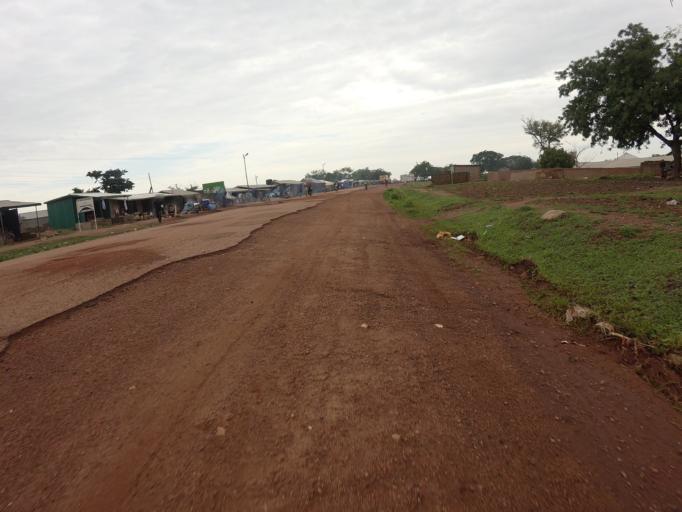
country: GH
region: Upper East
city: Bawku
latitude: 10.9342
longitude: -0.4990
